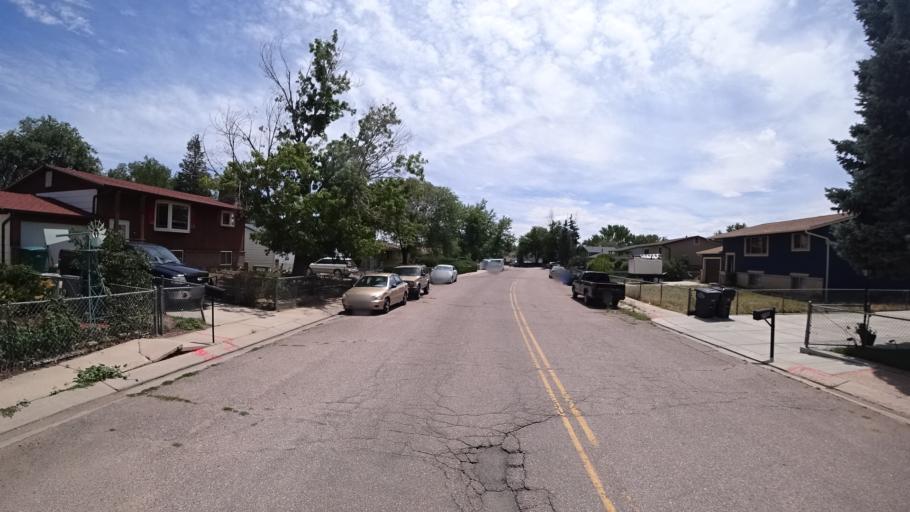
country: US
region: Colorado
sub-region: El Paso County
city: Security-Widefield
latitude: 38.7298
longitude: -104.7286
